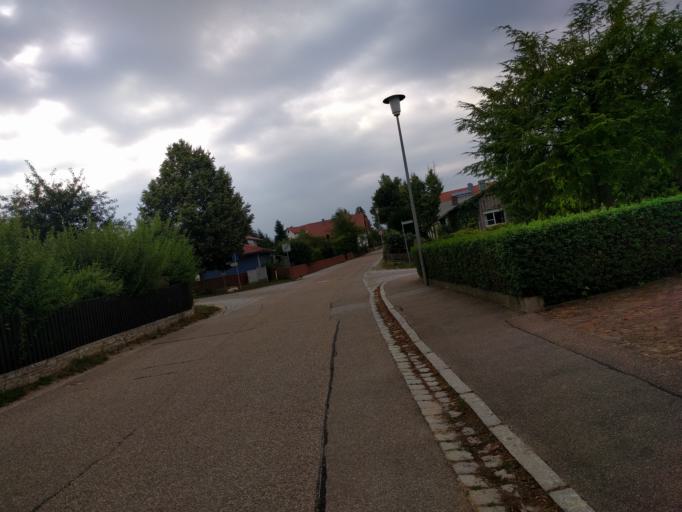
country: DE
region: Bavaria
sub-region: Upper Palatinate
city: Brunn
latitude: 49.0730
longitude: 11.8785
